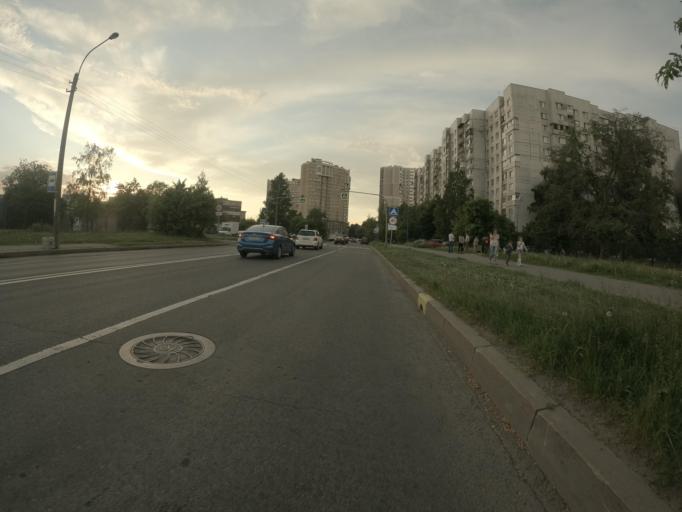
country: RU
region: St.-Petersburg
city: Kupchino
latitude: 59.8380
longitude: 30.3110
